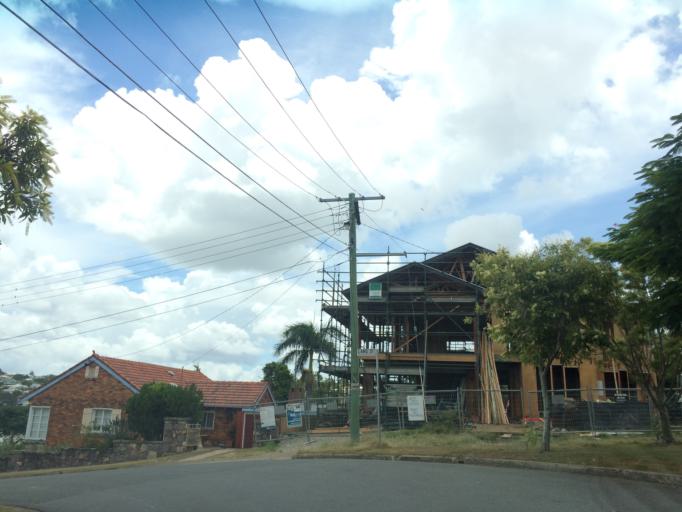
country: AU
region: Queensland
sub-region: Brisbane
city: Balmoral
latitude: -27.4463
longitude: 153.0590
